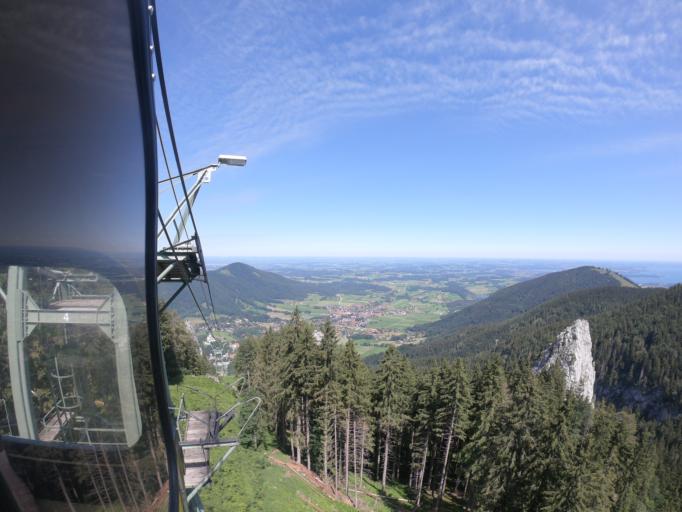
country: DE
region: Bavaria
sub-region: Upper Bavaria
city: Aschau im Chiemgau
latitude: 47.7569
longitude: 12.3435
